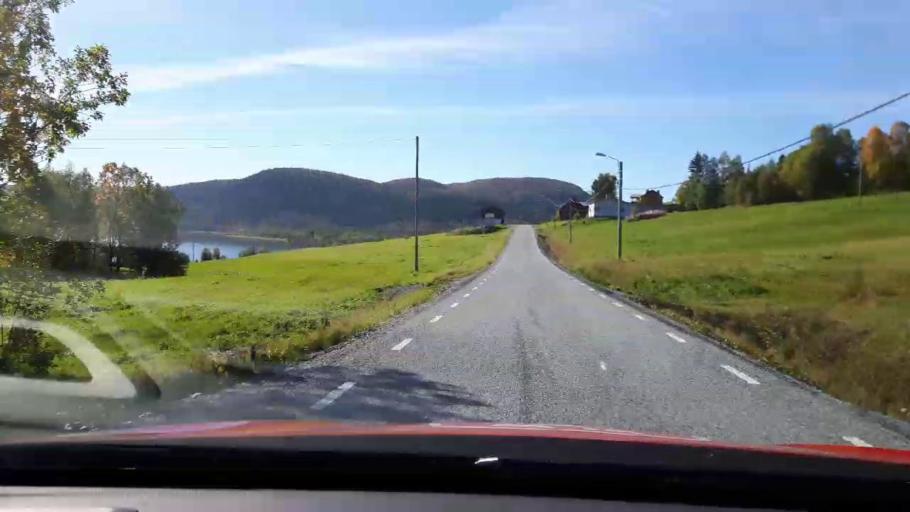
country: NO
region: Nord-Trondelag
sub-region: Royrvik
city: Royrvik
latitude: 64.7292
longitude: 13.9867
